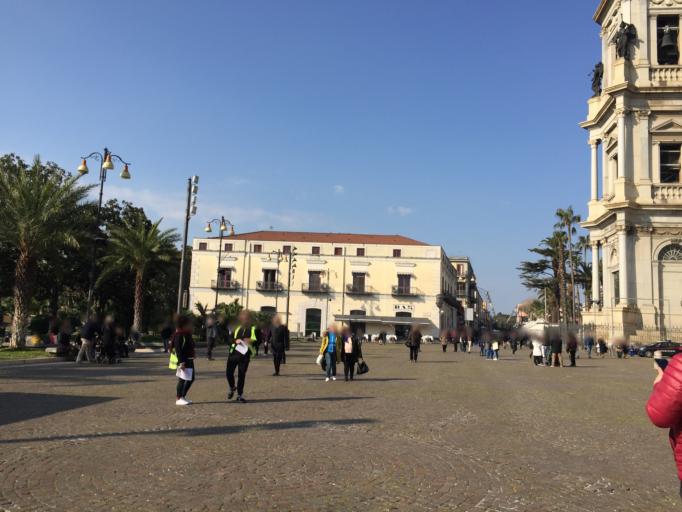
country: IT
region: Campania
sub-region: Provincia di Napoli
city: Pompei
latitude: 40.7495
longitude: 14.5009
